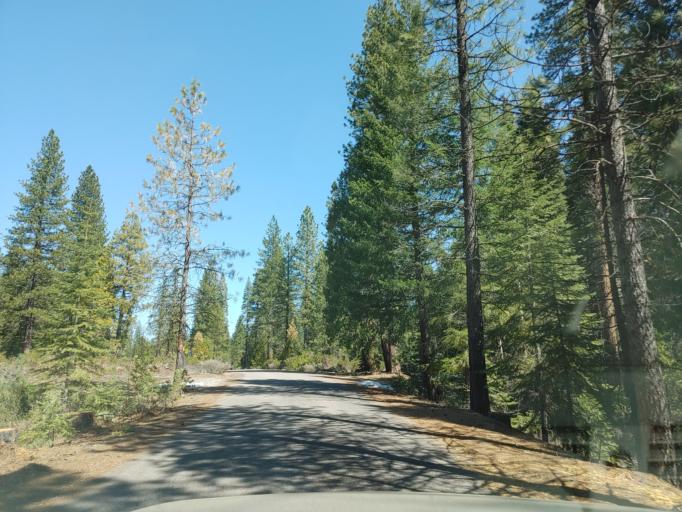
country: US
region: California
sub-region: Siskiyou County
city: McCloud
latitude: 41.2454
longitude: -121.9624
